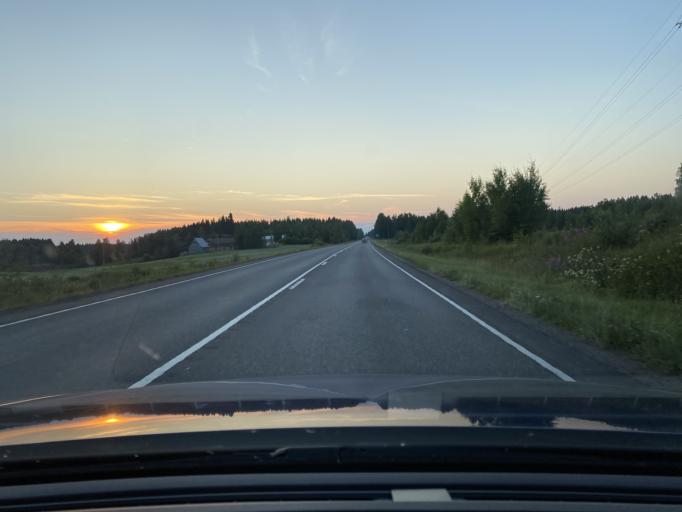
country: FI
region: Pirkanmaa
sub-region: Luoteis-Pirkanmaa
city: Ikaalinen
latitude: 61.8216
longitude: 22.9490
